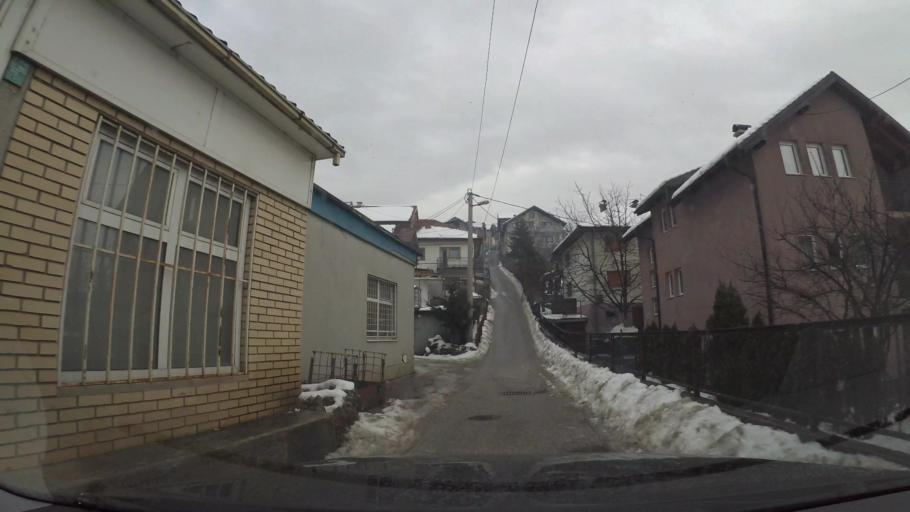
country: BA
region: Federation of Bosnia and Herzegovina
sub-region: Kanton Sarajevo
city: Sarajevo
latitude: 43.8542
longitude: 18.3451
